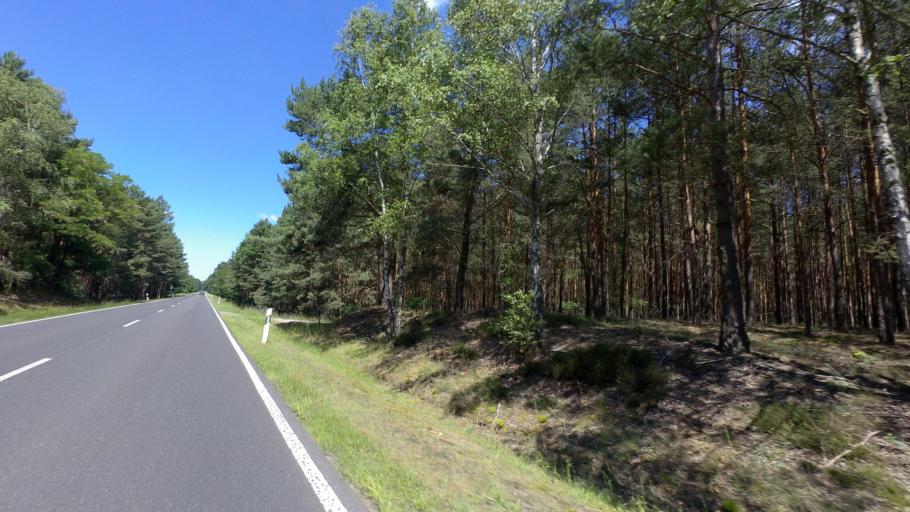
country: DE
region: Brandenburg
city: Baruth
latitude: 52.0105
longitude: 13.5505
